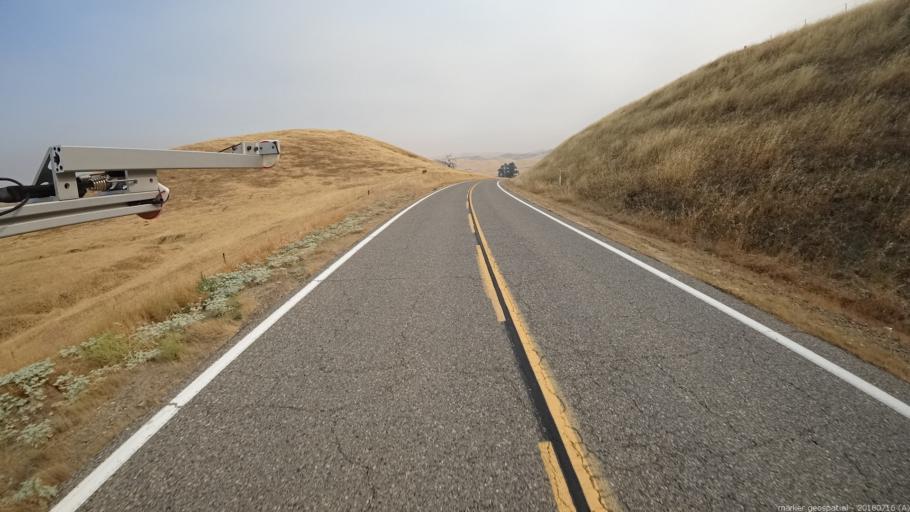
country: US
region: California
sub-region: Madera County
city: Madera Acres
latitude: 37.1911
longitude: -120.0036
